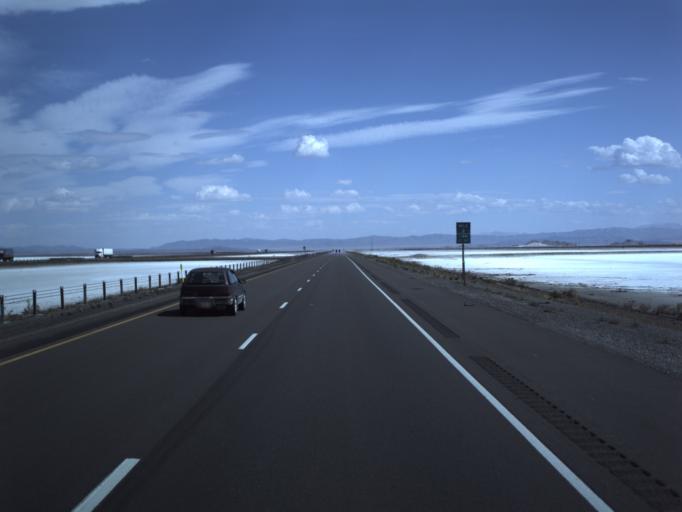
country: US
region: Utah
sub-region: Tooele County
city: Wendover
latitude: 40.7287
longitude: -113.4080
